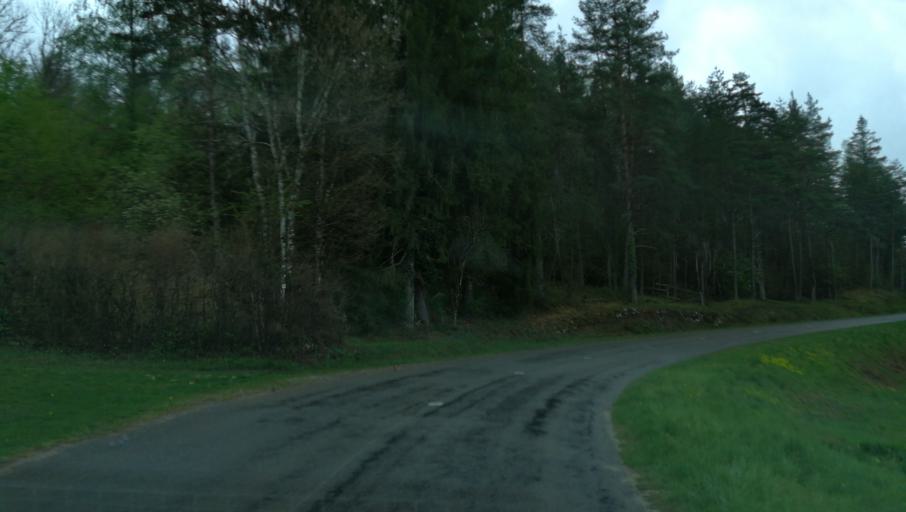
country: FR
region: Franche-Comte
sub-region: Departement du Jura
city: Moirans-en-Montagne
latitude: 46.4647
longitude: 5.7020
